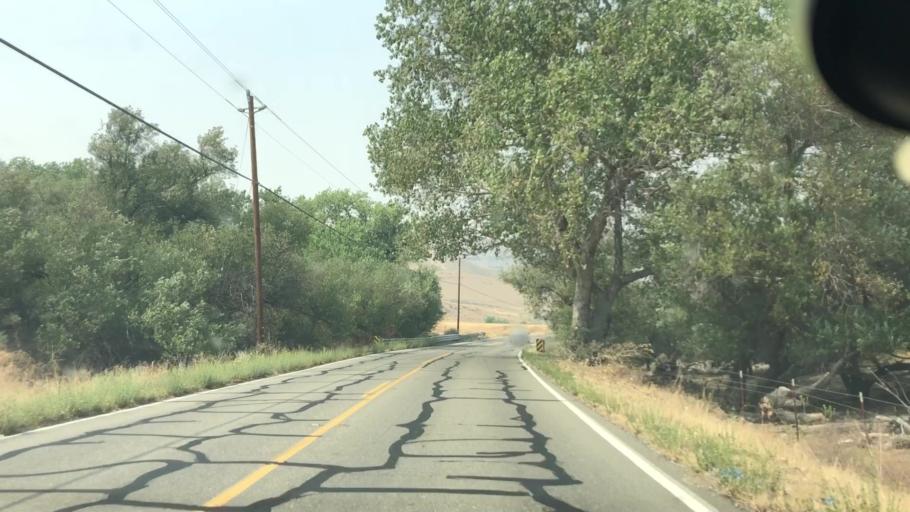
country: US
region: California
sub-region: San Joaquin County
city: Tracy
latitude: 37.6463
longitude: -121.4910
